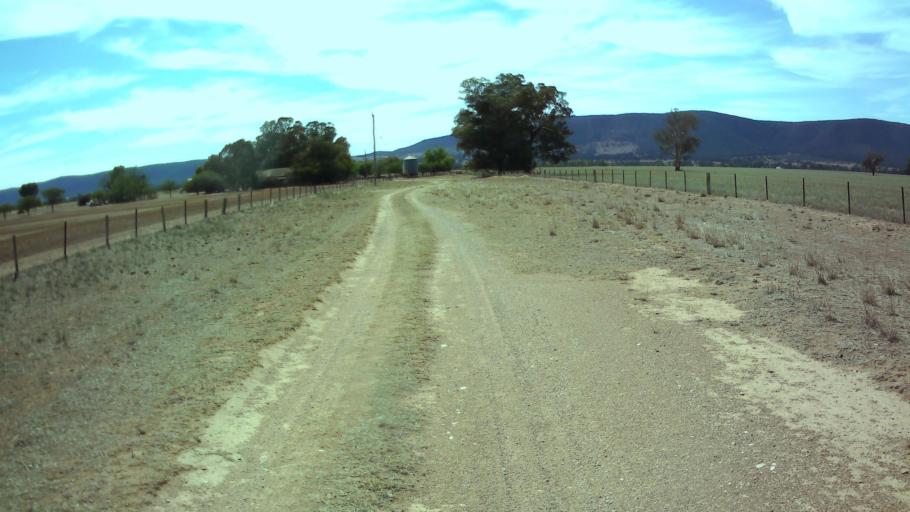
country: AU
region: New South Wales
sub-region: Weddin
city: Grenfell
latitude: -33.7224
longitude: 148.2723
